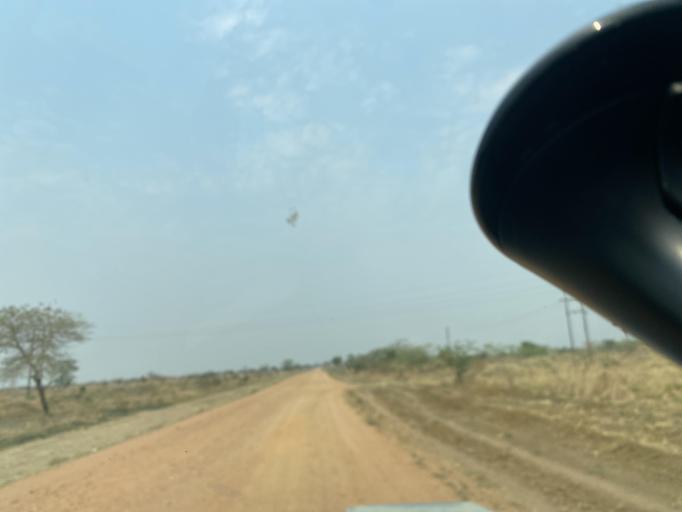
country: ZM
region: Lusaka
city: Kafue
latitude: -15.6771
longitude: 28.0143
